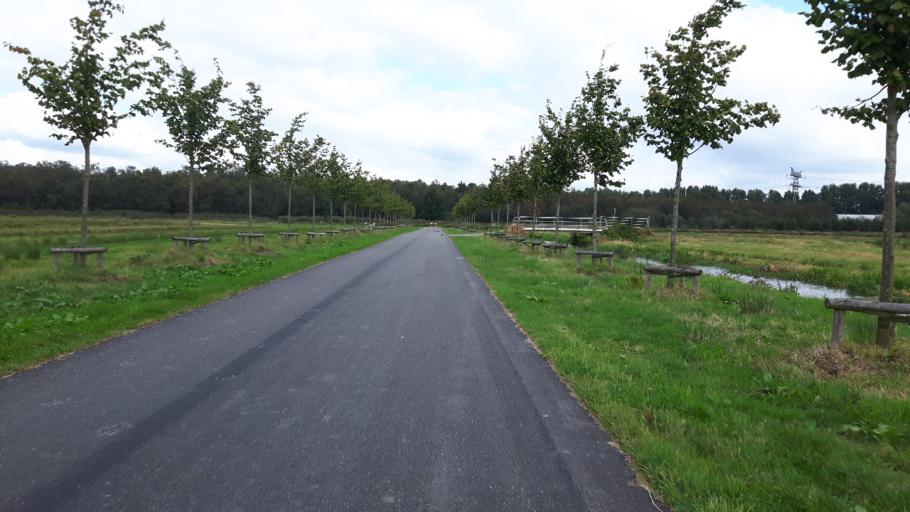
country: NL
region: Utrecht
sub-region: Stichtse Vecht
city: Spechtenkamp
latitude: 52.1274
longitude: 5.0087
